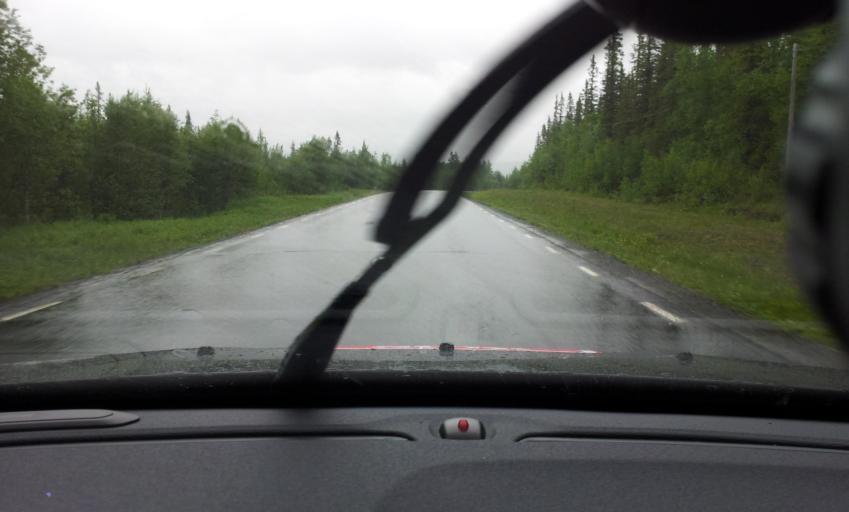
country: SE
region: Jaemtland
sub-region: Are Kommun
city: Are
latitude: 63.2679
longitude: 13.2196
